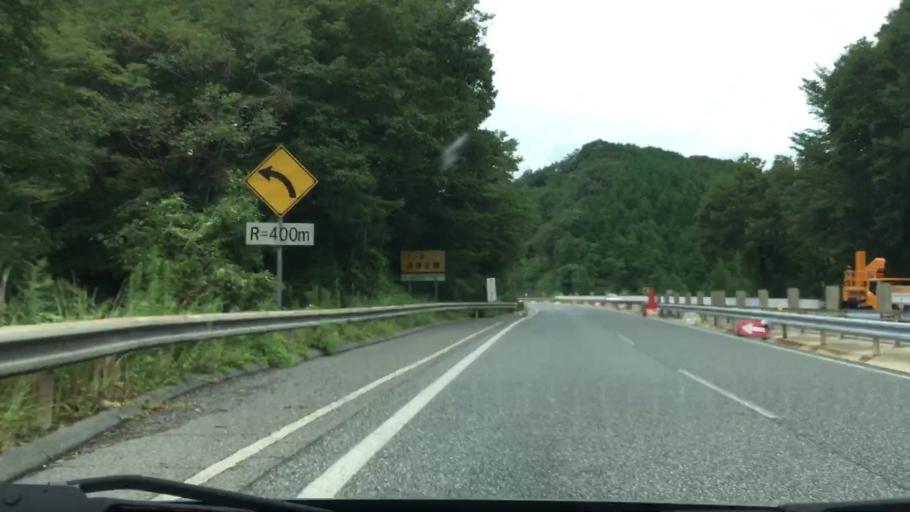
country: JP
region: Okayama
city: Niimi
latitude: 35.0165
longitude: 133.5839
